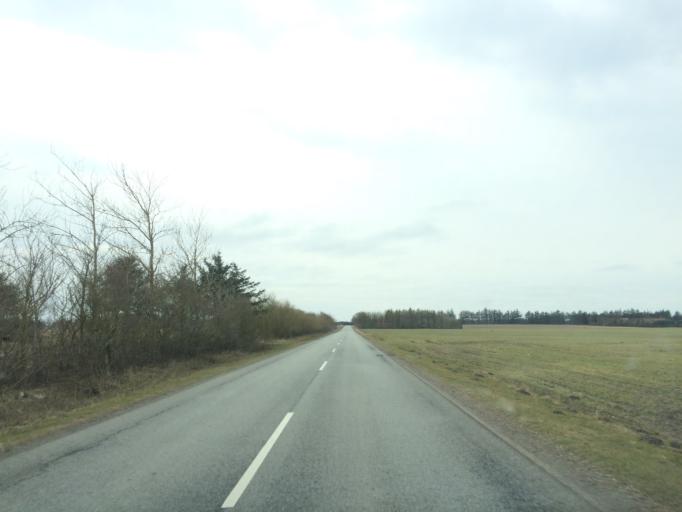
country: DK
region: Central Jutland
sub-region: Ringkobing-Skjern Kommune
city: Tarm
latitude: 55.8399
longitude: 8.4670
